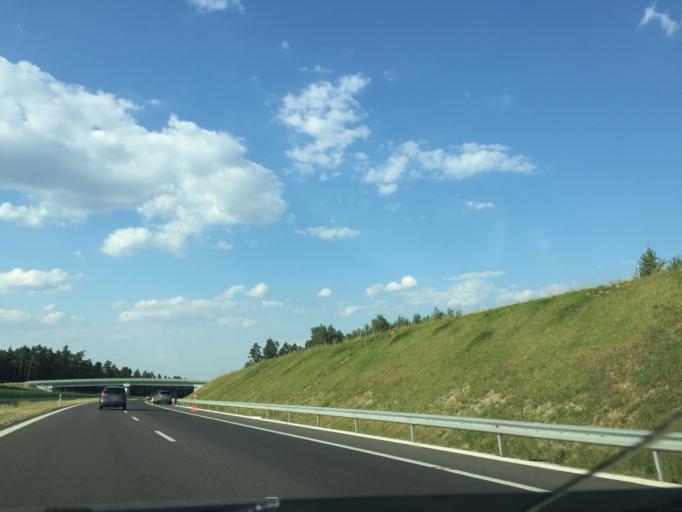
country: PL
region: Swietokrzyskie
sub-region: Powiat skarzyski
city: Skarzysko-Kamienna
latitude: 51.1413
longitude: 20.8327
